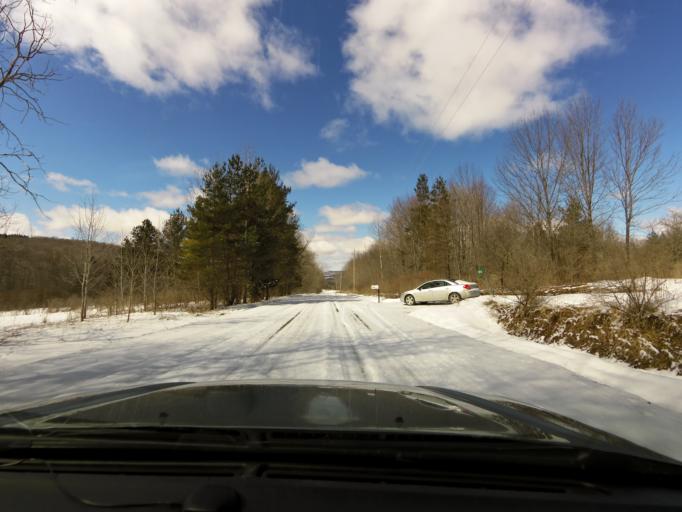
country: US
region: New York
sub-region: Cattaraugus County
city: Franklinville
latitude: 42.3428
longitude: -78.4048
